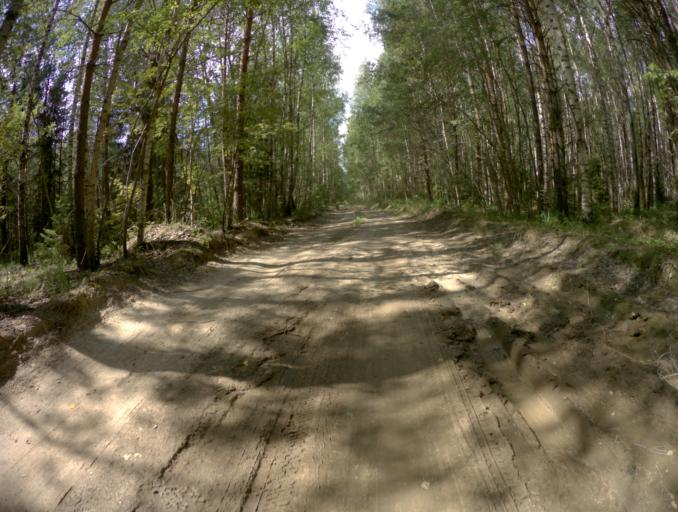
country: RU
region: Vladimir
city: Raduzhnyy
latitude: 55.9674
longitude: 40.2286
